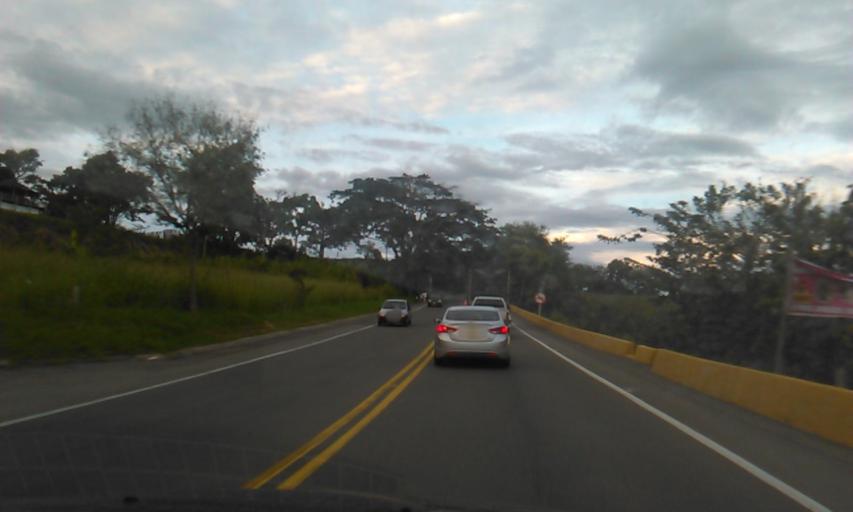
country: CO
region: Quindio
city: La Tebaida
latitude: 4.4308
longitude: -75.8604
